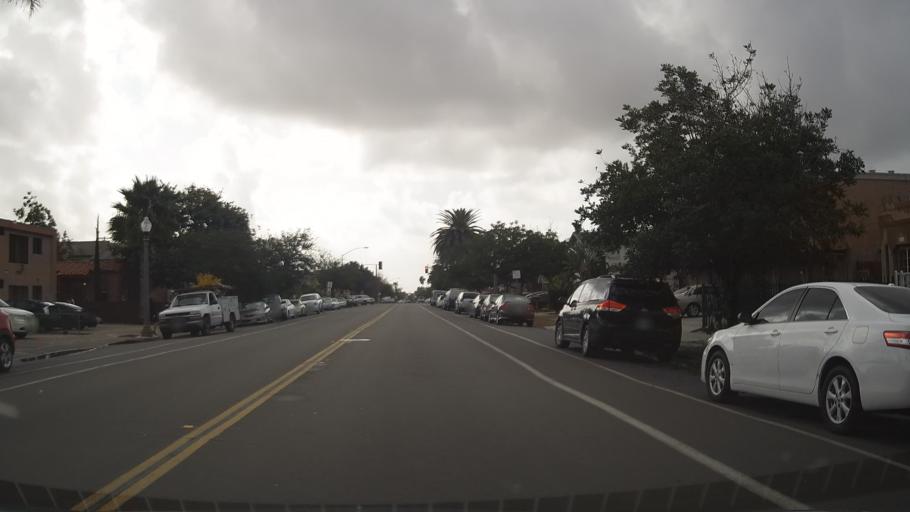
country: US
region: California
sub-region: San Diego County
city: San Diego
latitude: 32.7547
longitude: -117.1180
